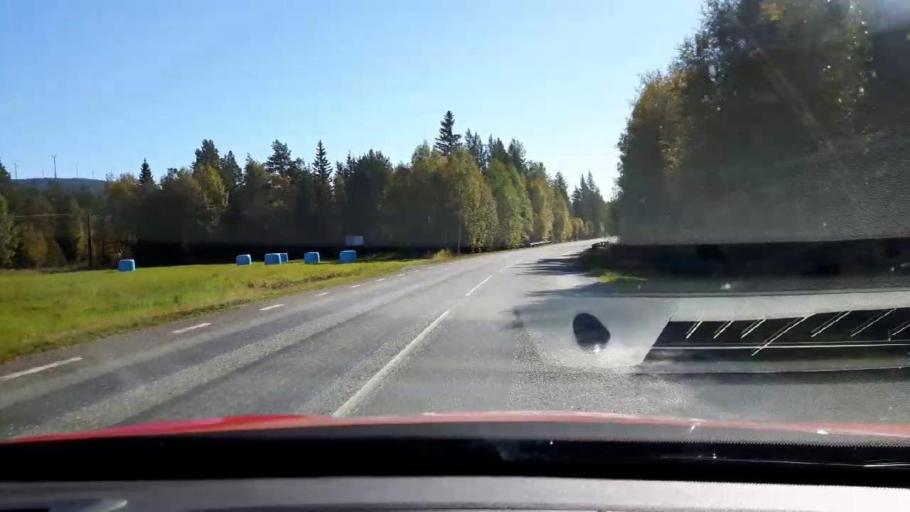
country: SE
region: Jaemtland
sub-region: Harjedalens Kommun
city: Sveg
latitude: 62.3525
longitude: 14.0269
